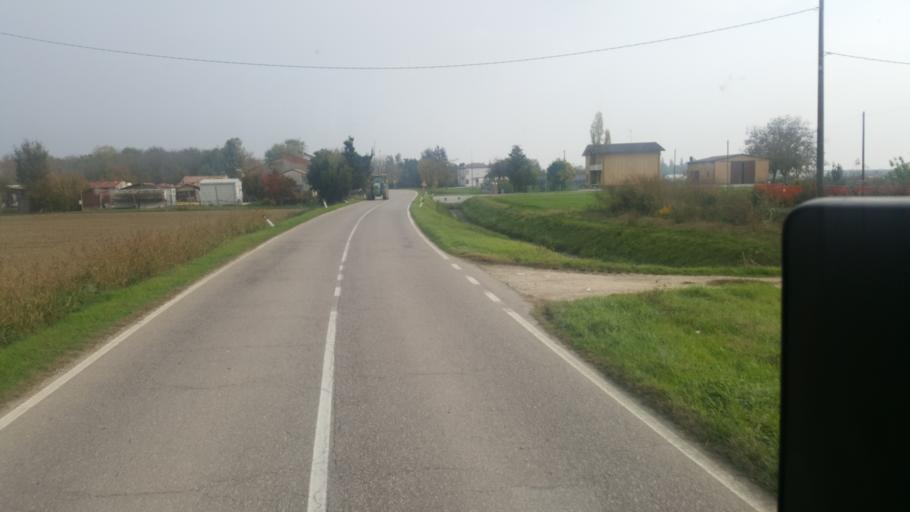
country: IT
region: Lombardy
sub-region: Provincia di Mantova
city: Felonica
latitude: 44.9458
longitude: 11.3067
